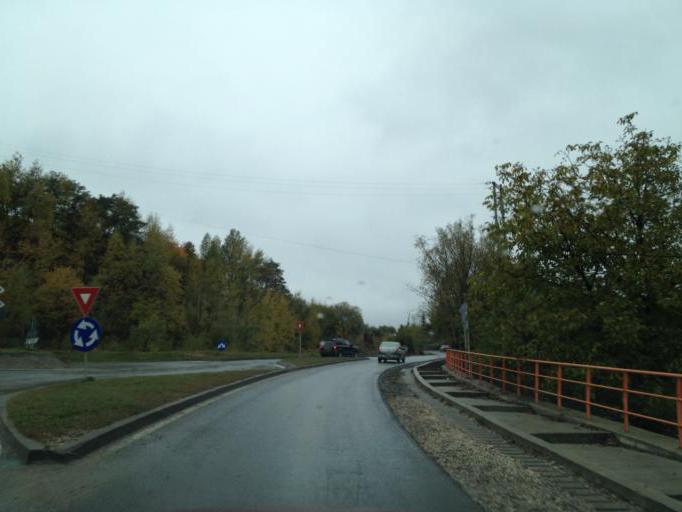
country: RO
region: Arges
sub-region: Comuna Valea Mare-Pravat
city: Valea Mare Pravat
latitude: 45.2958
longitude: 25.1083
